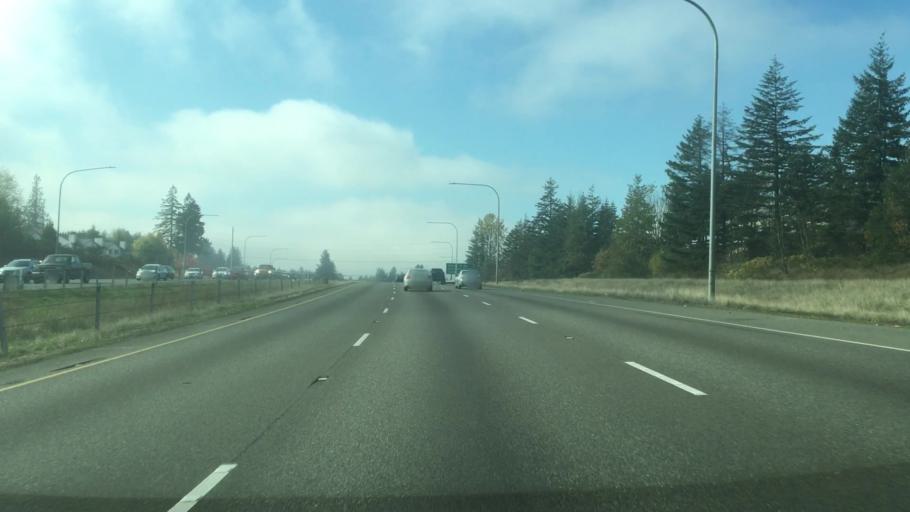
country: US
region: Washington
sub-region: Thurston County
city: Olympia
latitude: 47.0259
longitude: -122.9155
